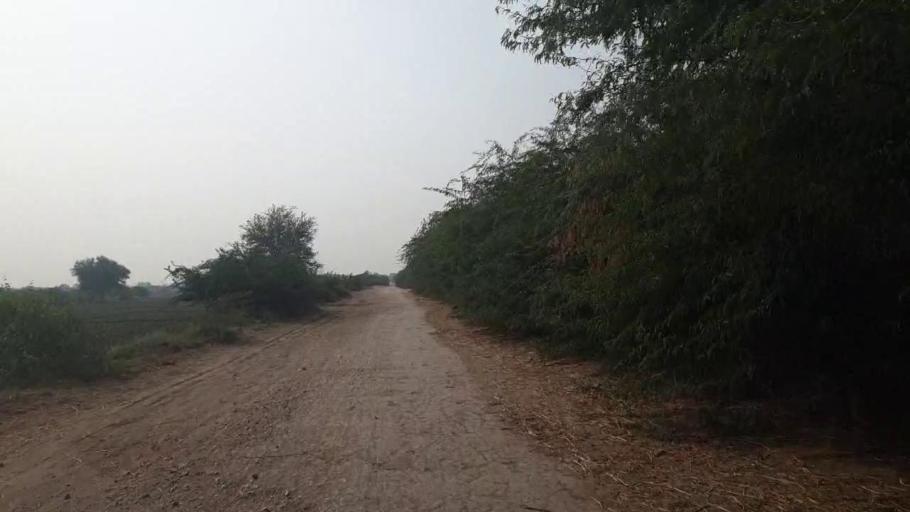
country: PK
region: Sindh
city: Tando Jam
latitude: 25.2860
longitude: 68.4965
